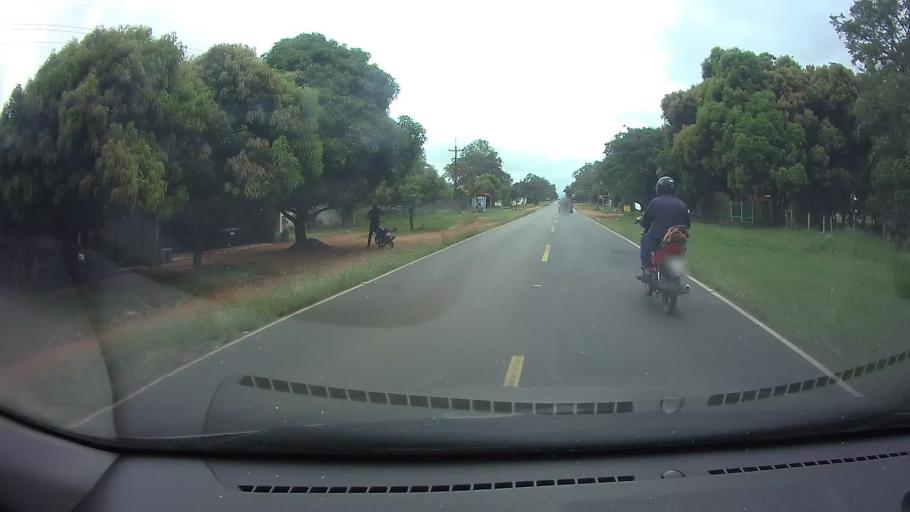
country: PY
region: Central
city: Nueva Italia
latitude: -25.5755
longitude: -57.5050
